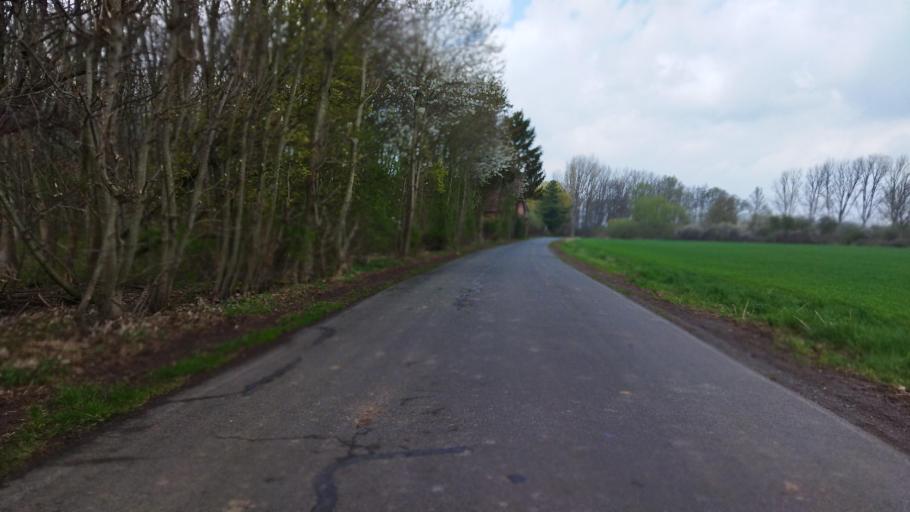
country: DE
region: Lower Saxony
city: Hilgermissen
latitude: 52.8305
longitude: 9.1902
